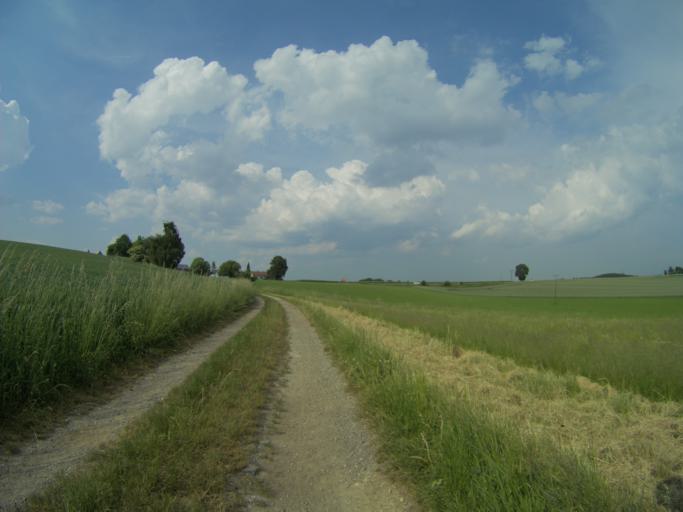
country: DE
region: Bavaria
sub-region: Upper Bavaria
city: Marzling
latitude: 48.4328
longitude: 11.8004
